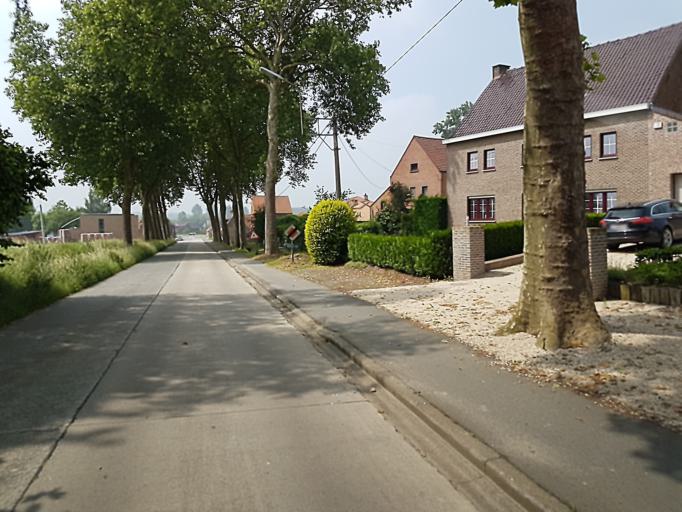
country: BE
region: Flanders
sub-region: Provincie Oost-Vlaanderen
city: Sint-Maria-Lierde
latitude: 50.8083
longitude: 3.8750
